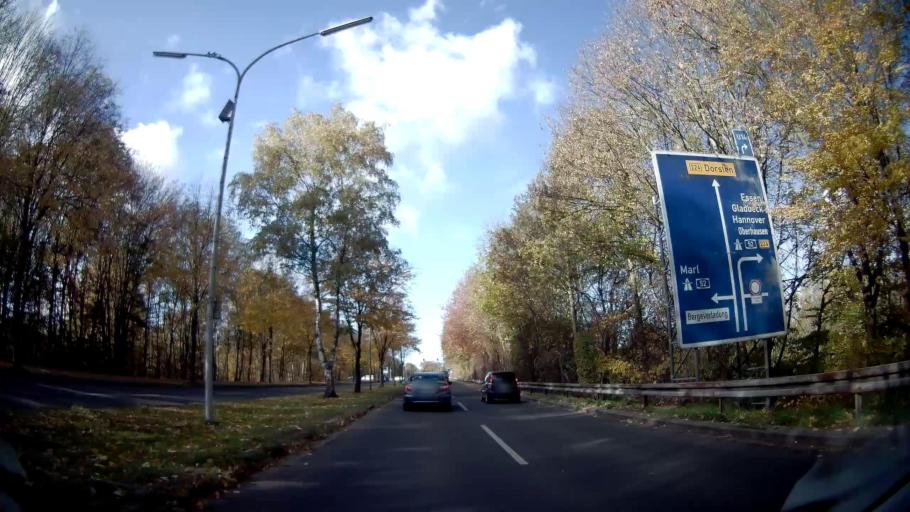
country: DE
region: North Rhine-Westphalia
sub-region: Regierungsbezirk Munster
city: Gladbeck
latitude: 51.6096
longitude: 7.0378
